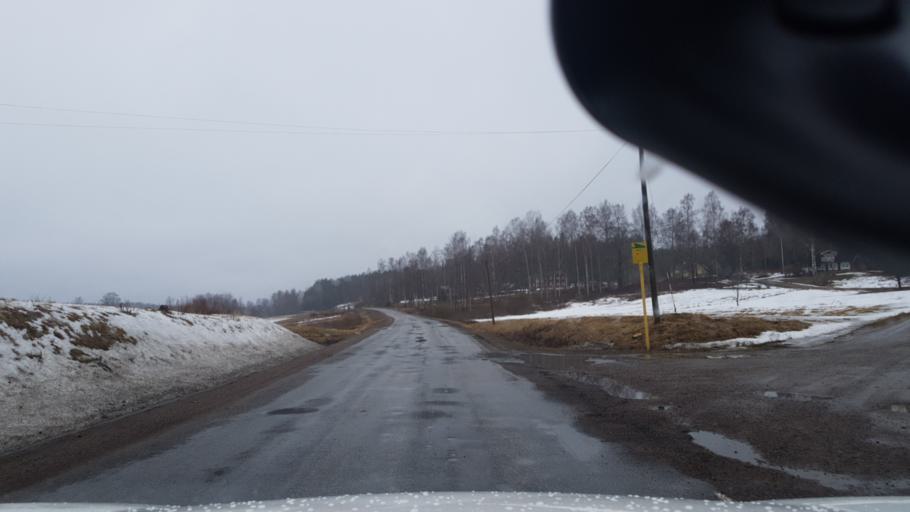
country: SE
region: Vaermland
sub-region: Arvika Kommun
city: Arvika
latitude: 59.6604
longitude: 12.7134
